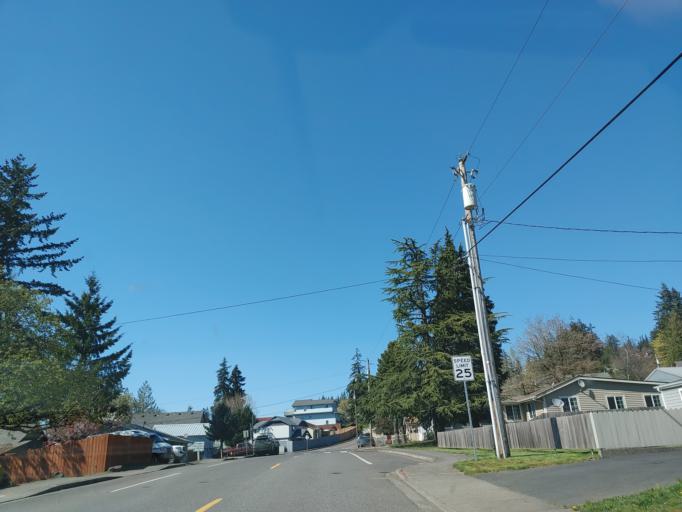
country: US
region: Washington
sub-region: Cowlitz County
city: Kalama
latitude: 46.0101
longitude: -122.8407
